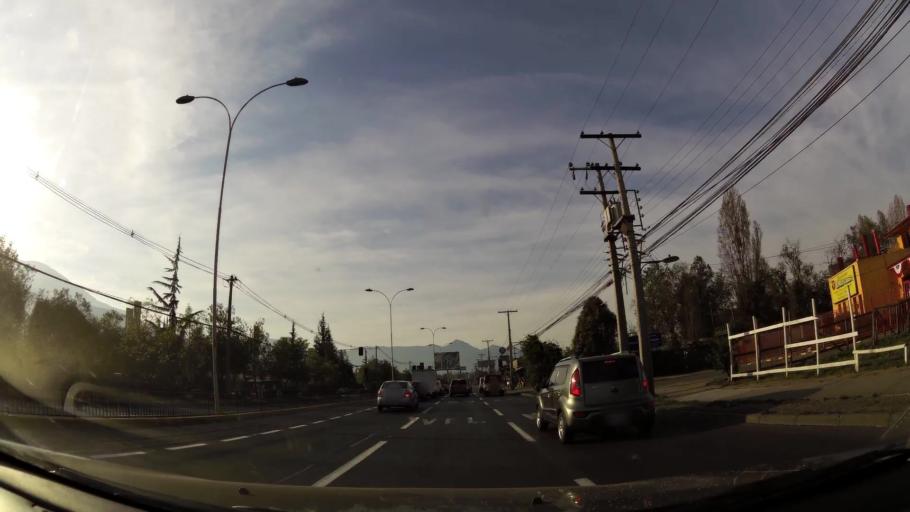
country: CL
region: Santiago Metropolitan
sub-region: Provincia de Cordillera
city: Puente Alto
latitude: -33.5548
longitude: -70.5624
